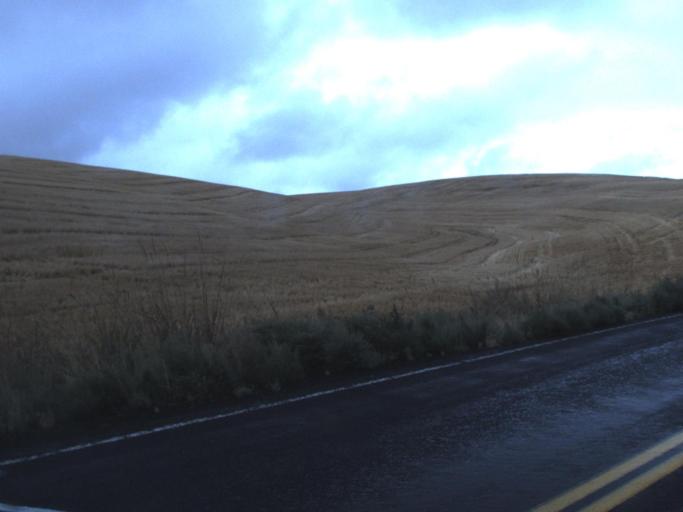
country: US
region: Washington
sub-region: Spokane County
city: Cheney
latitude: 47.1551
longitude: -117.8515
